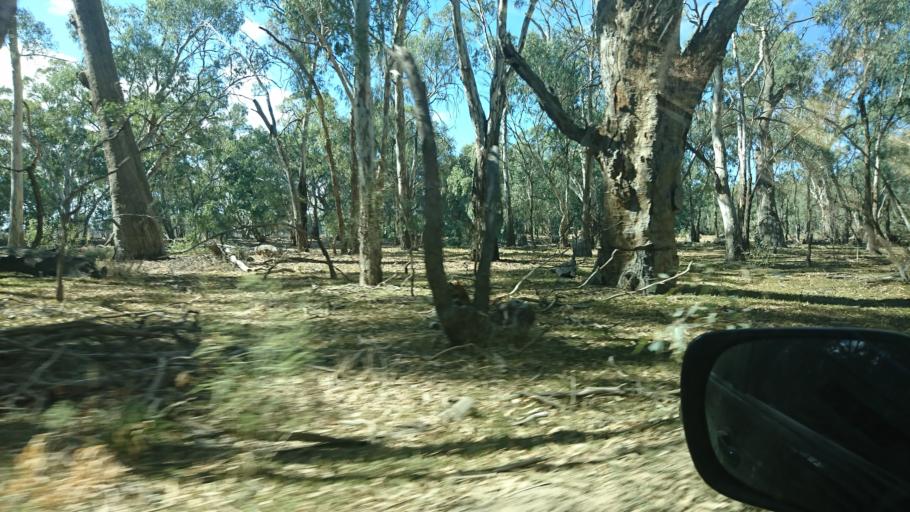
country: AU
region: Victoria
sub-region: Swan Hill
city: Swan Hill
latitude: -35.1415
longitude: 143.3860
